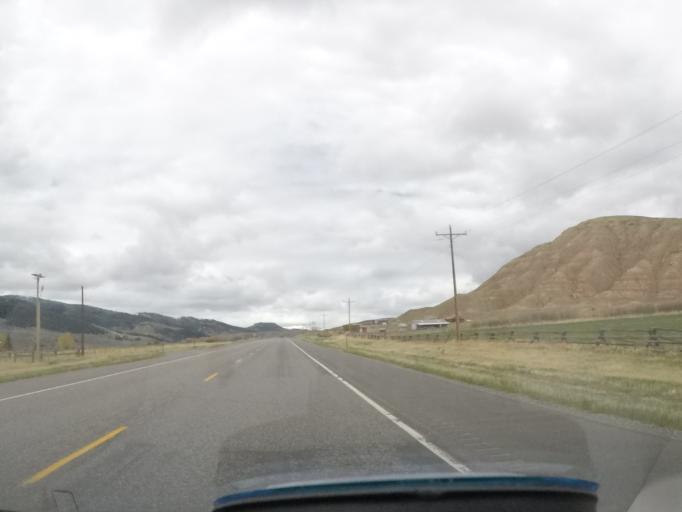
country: US
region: Wyoming
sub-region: Sublette County
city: Pinedale
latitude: 43.5698
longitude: -109.7159
